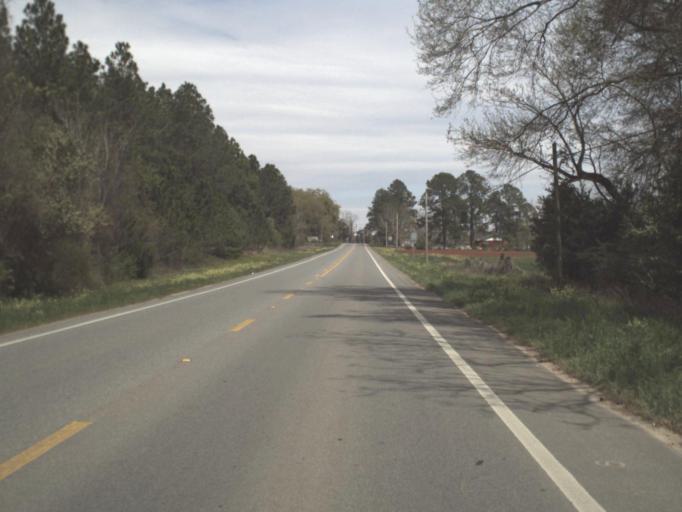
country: US
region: Florida
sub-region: Jackson County
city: Graceville
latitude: 30.9453
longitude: -85.4067
